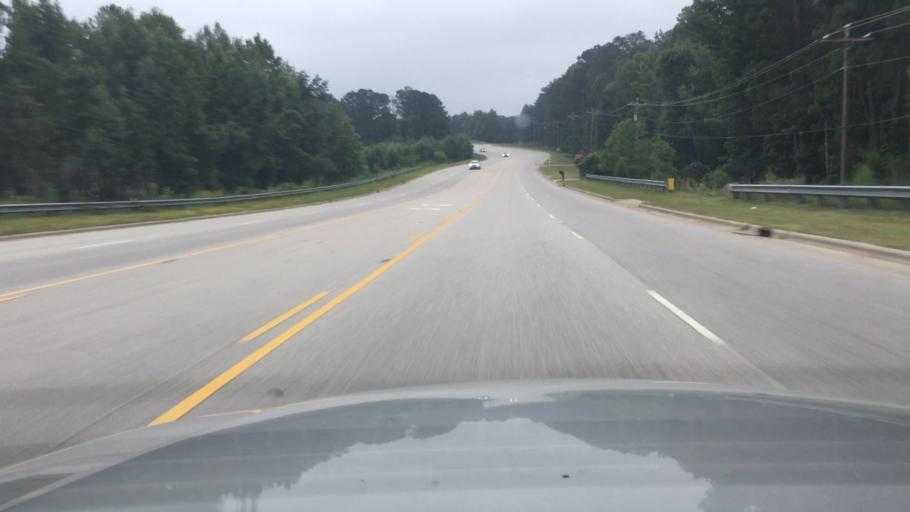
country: US
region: North Carolina
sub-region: Cumberland County
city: Fayetteville
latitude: 35.0100
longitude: -78.8763
